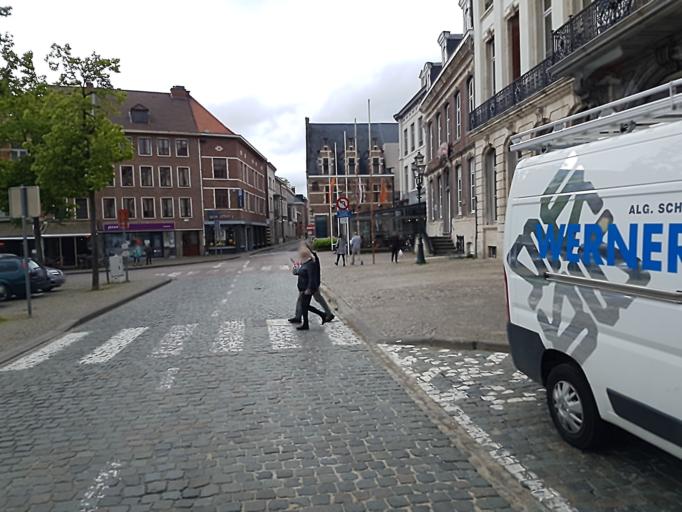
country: BE
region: Flanders
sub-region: Provincie Vlaams-Brabant
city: Tienen
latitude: 50.8079
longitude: 4.9366
